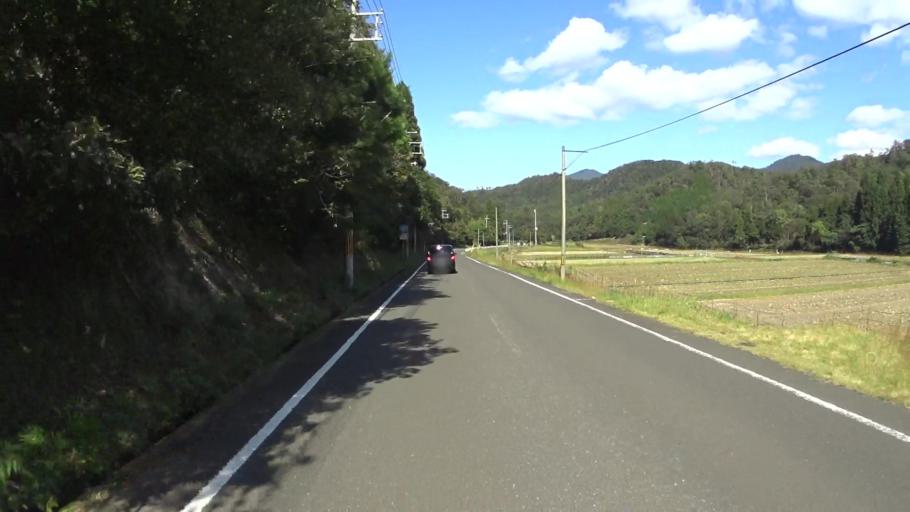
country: JP
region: Hyogo
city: Toyooka
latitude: 35.5545
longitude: 134.9775
